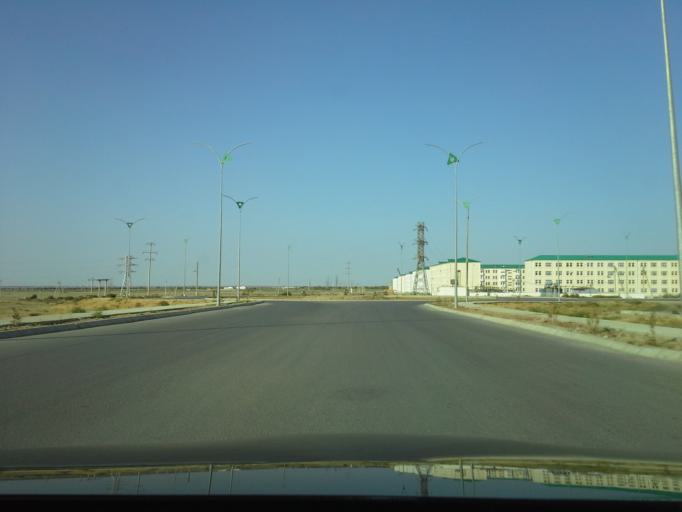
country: TM
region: Ahal
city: Abadan
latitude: 38.0564
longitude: 58.1383
